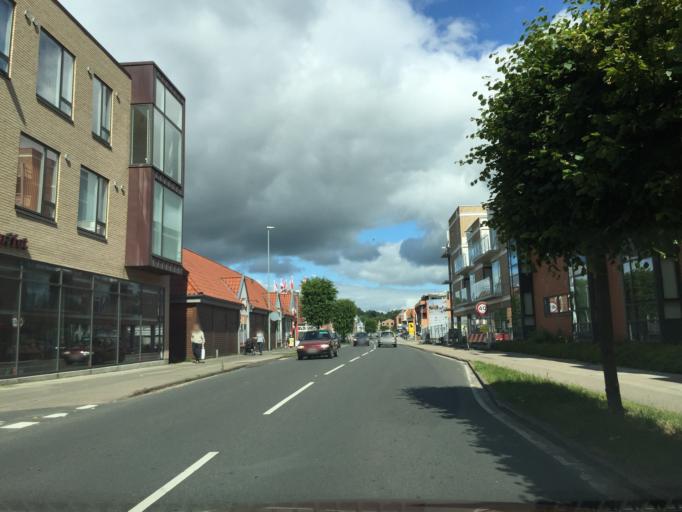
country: DK
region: Central Jutland
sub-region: Silkeborg Kommune
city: Silkeborg
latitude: 56.1802
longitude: 9.5502
